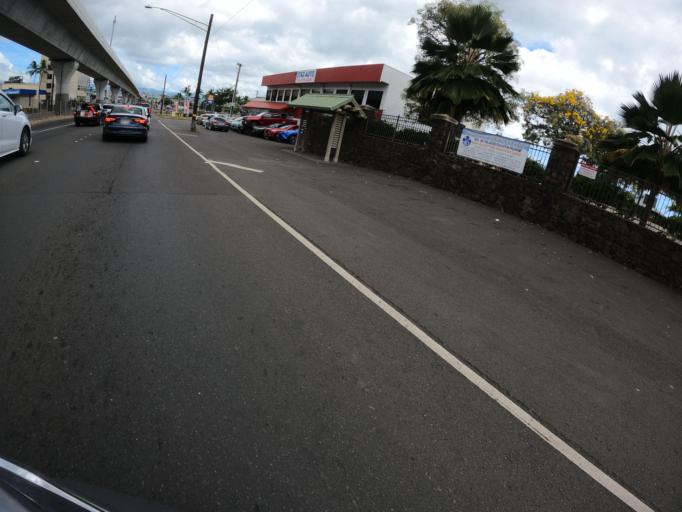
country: US
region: Hawaii
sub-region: Honolulu County
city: Waipahu
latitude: 21.3830
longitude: -158.0077
